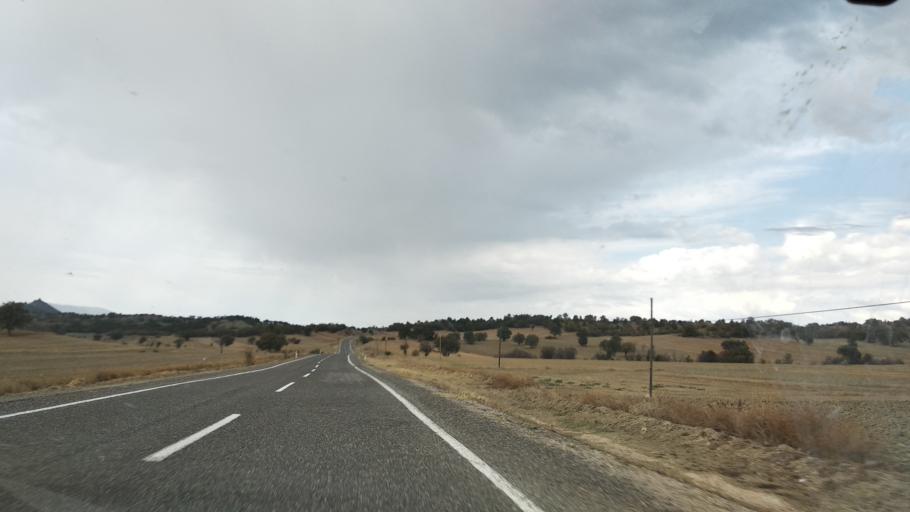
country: TR
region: Bolu
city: Seben
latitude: 40.3330
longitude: 31.4524
